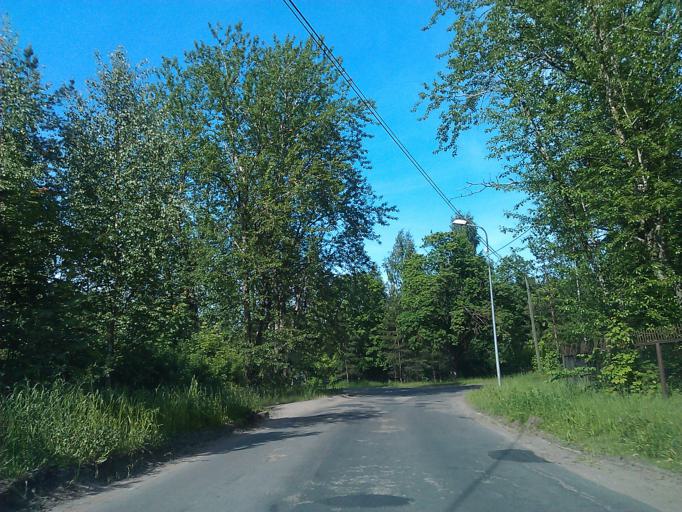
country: LV
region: Riga
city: Jaunciems
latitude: 56.9908
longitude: 24.2085
